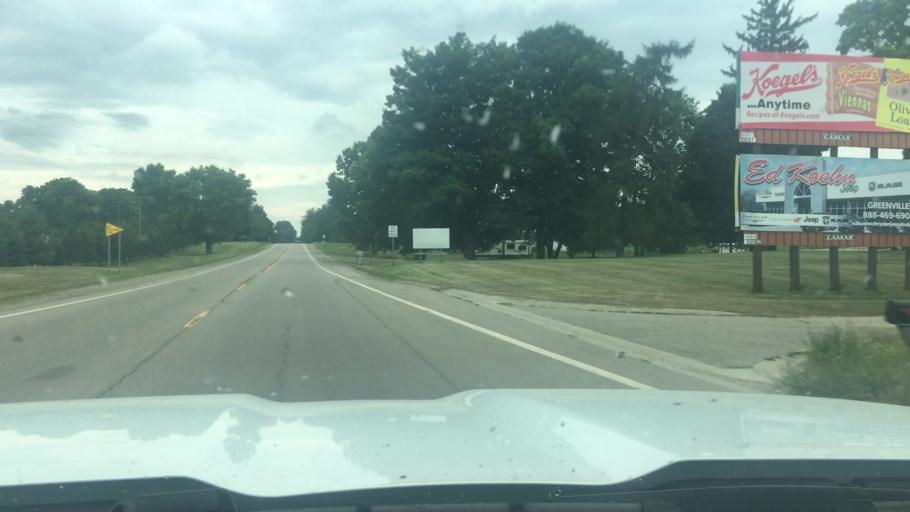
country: US
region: Michigan
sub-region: Ionia County
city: Ionia
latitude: 43.0019
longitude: -84.9958
